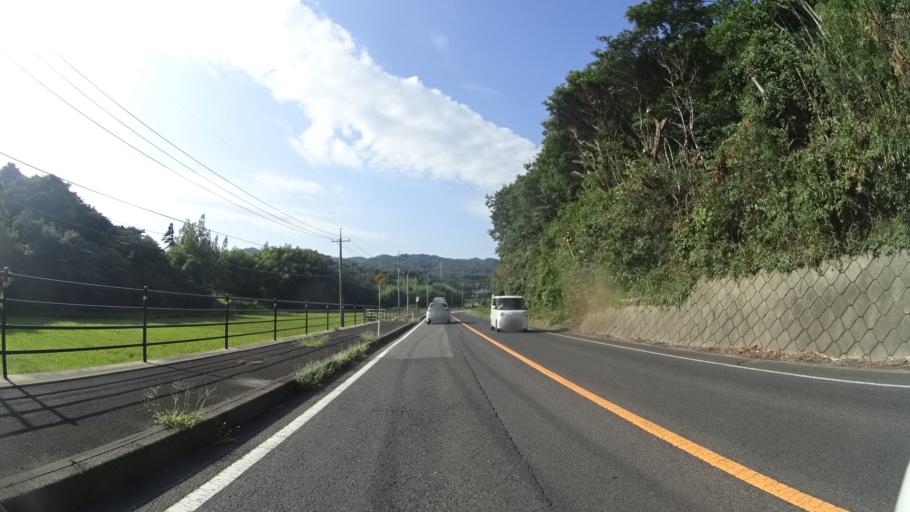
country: JP
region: Shimane
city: Izumo
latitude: 35.2978
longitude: 132.6486
